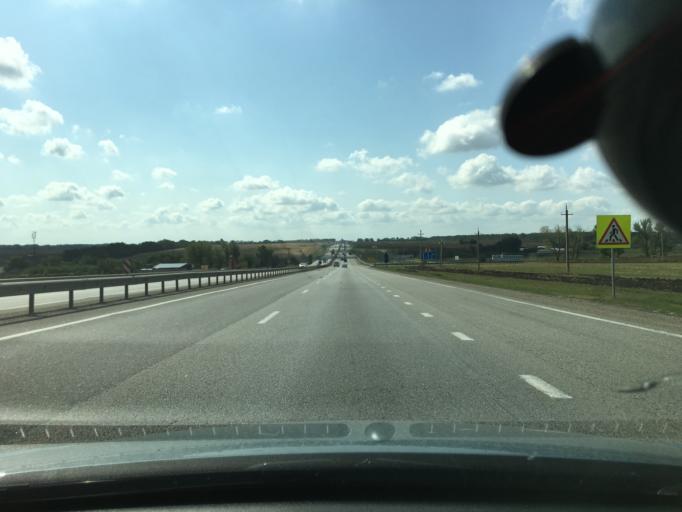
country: RU
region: Krasnodarskiy
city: Krasnoye
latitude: 46.7734
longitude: 39.6634
